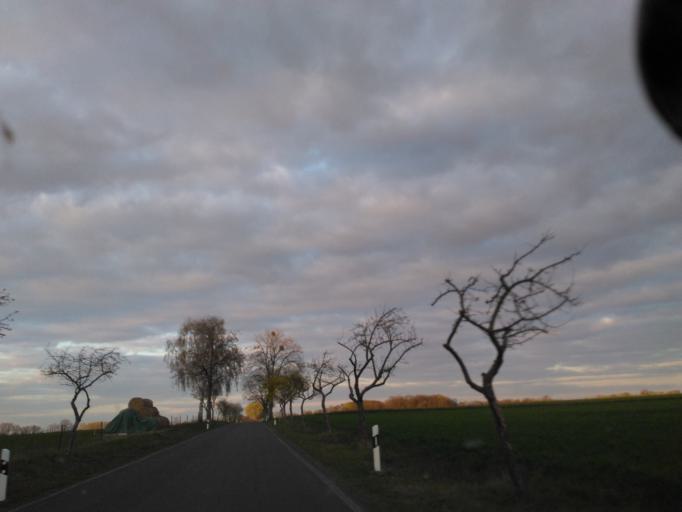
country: DE
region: Brandenburg
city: Buckow
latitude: 52.6156
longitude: 14.0565
